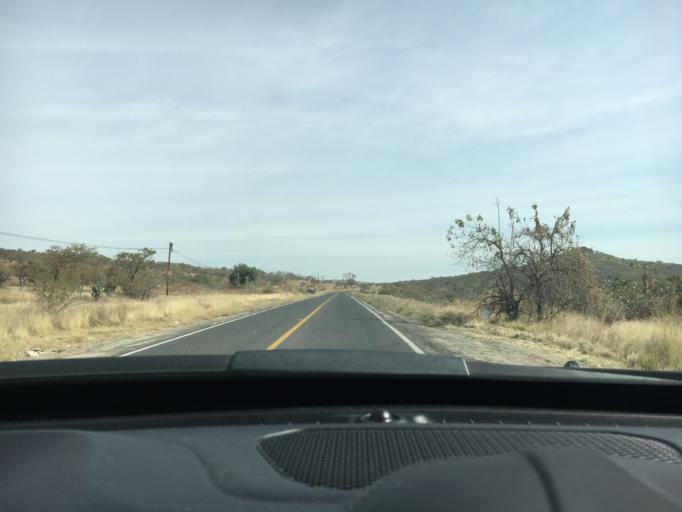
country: MX
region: Guanajuato
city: Duarte
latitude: 21.0615
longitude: -101.5040
